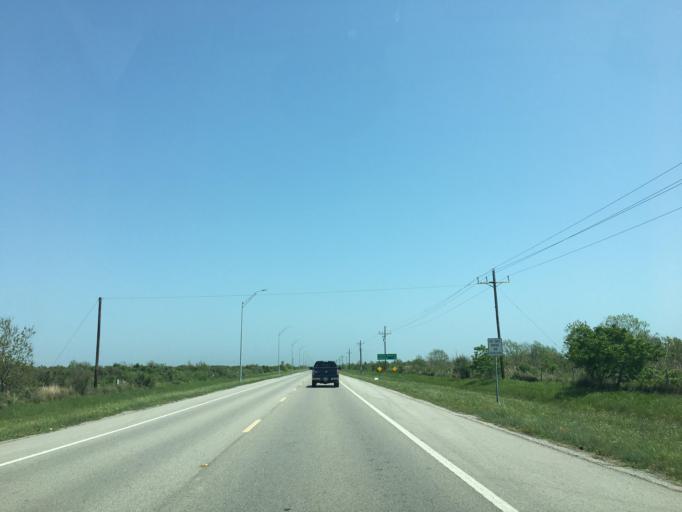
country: US
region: Texas
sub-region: Galveston County
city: Galveston
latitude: 29.3811
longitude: -94.7444
